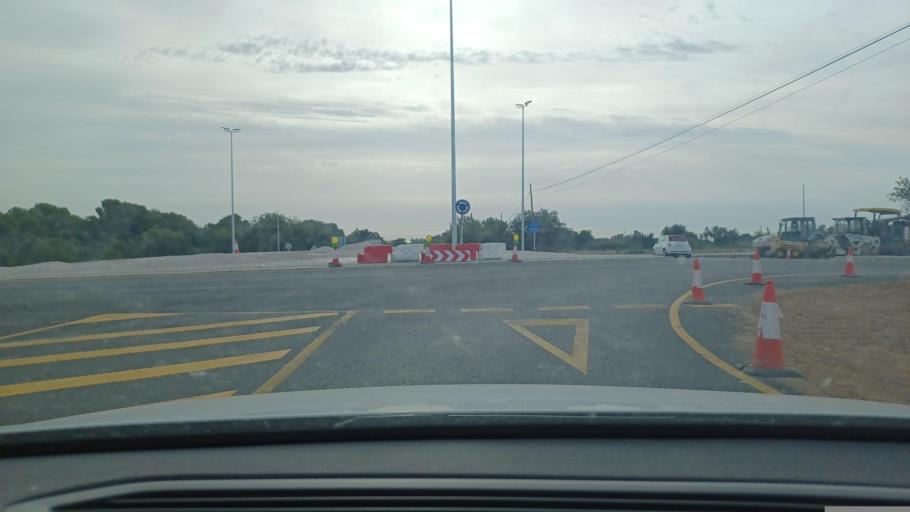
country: ES
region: Catalonia
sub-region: Provincia de Tarragona
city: Cambrils
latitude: 41.0771
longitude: 1.0413
